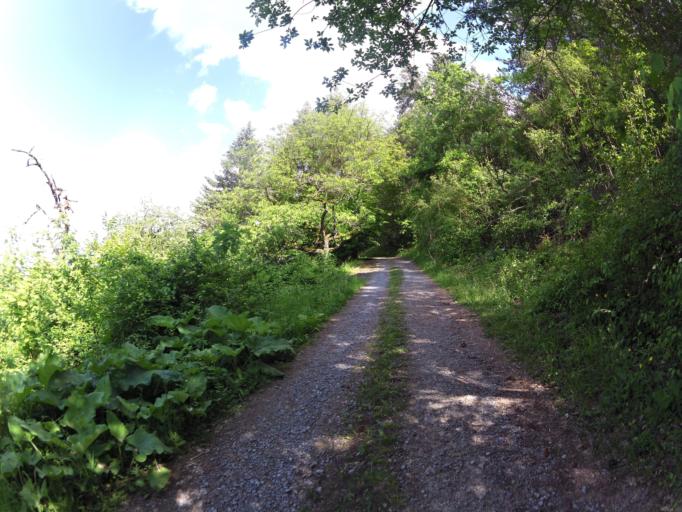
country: DE
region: Bavaria
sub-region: Regierungsbezirk Unterfranken
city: Erlabrunn
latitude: 49.8661
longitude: 9.8305
